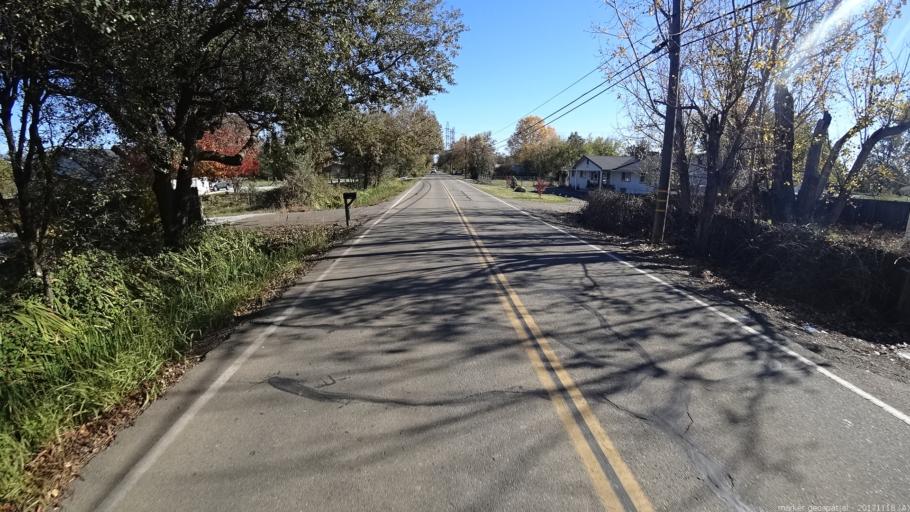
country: US
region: California
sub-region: Shasta County
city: Cottonwood
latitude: 40.3893
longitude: -122.2717
